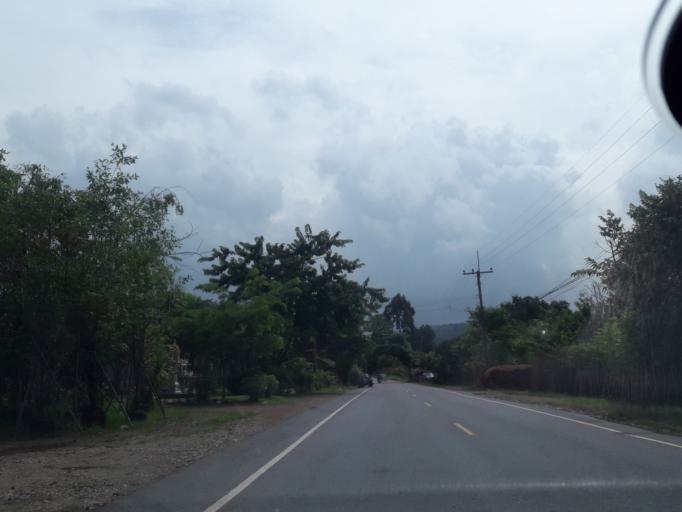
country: TH
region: Sara Buri
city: Wihan Daeng
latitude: 14.4199
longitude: 101.1223
